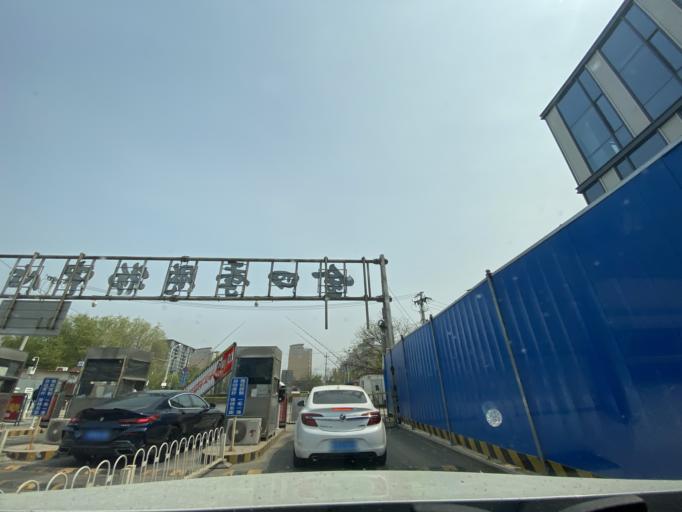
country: CN
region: Beijing
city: Sijiqing
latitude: 39.9417
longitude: 116.2671
